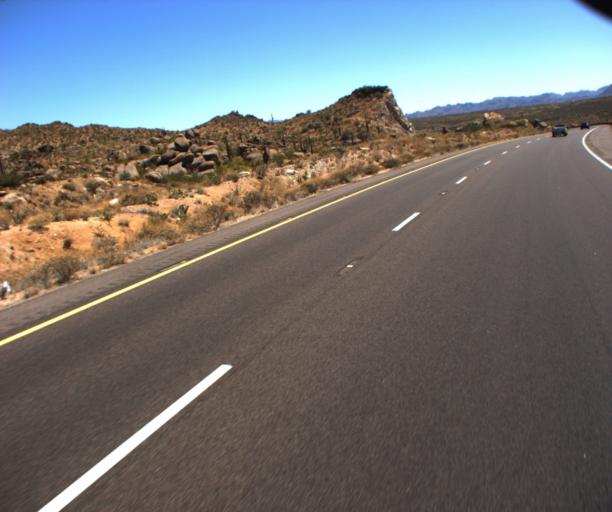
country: US
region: Arizona
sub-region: Maricopa County
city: Rio Verde
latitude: 33.6960
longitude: -111.5021
